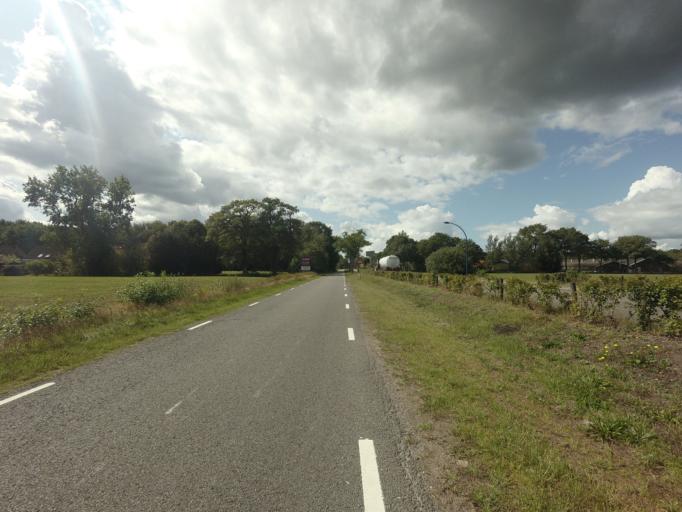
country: NL
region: Friesland
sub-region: Gemeente Heerenveen
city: Jubbega
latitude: 52.9581
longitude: 6.1891
